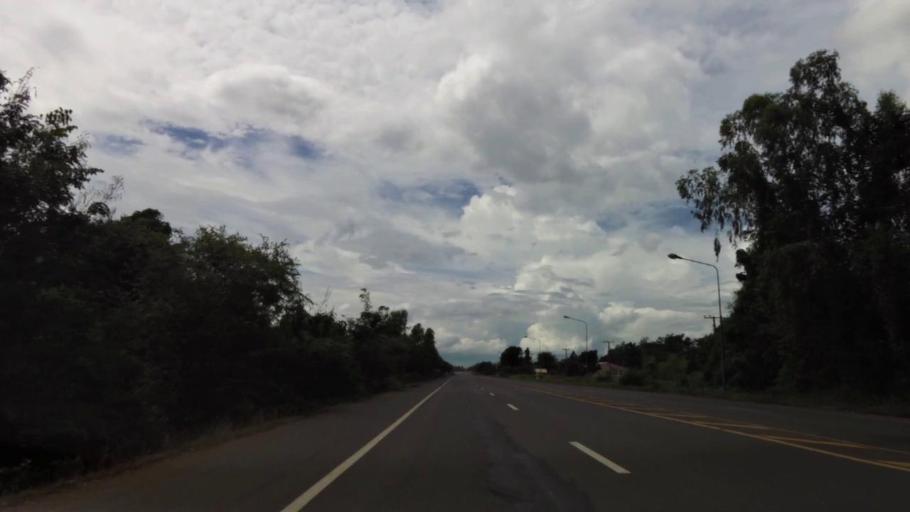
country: TH
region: Nakhon Sawan
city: Phai Sali
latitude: 15.5993
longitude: 100.6670
